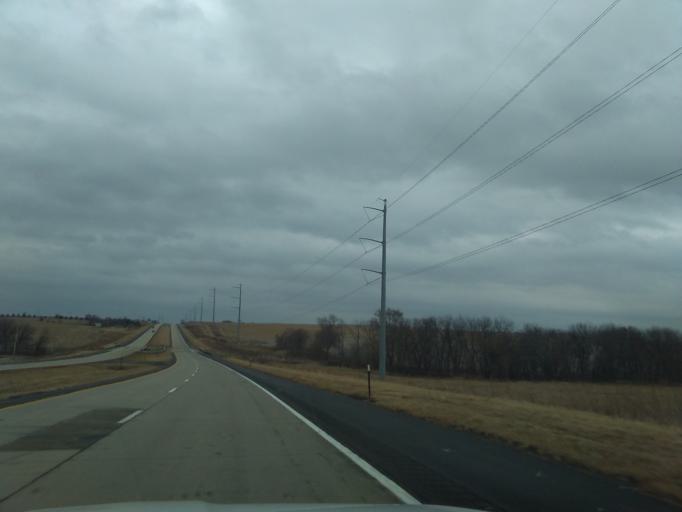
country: US
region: Nebraska
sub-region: Otoe County
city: Syracuse
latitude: 40.6682
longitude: -96.1518
